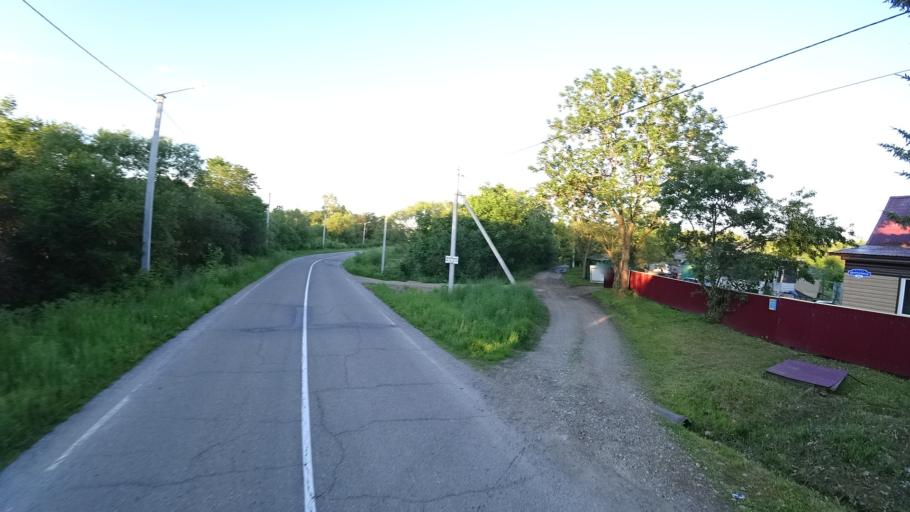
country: RU
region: Khabarovsk Krai
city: Khor
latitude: 47.8564
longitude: 134.9879
